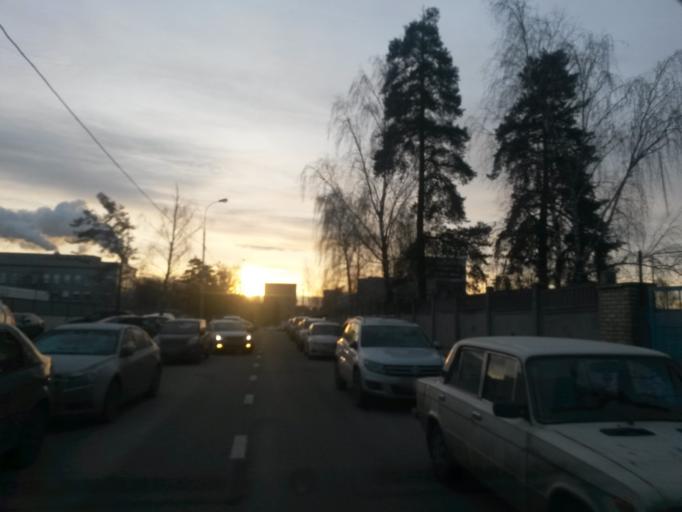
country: RU
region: Moskovskaya
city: Bol'shaya Setun'
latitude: 55.7039
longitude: 37.4228
